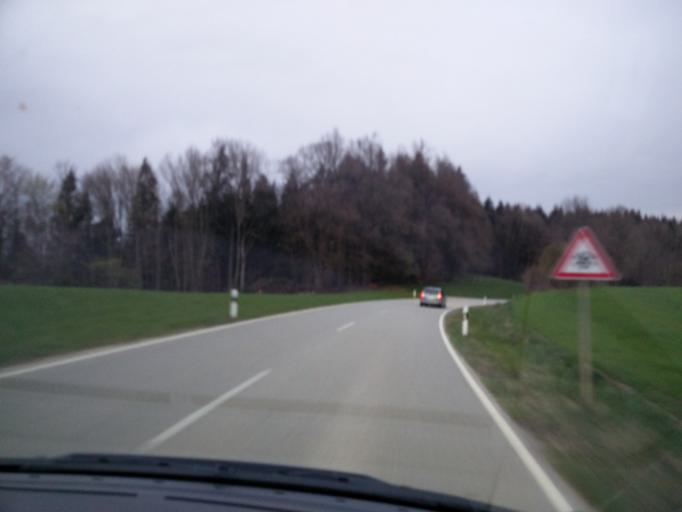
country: DE
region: Bavaria
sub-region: Upper Bavaria
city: Amerang
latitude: 47.9830
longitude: 12.2996
